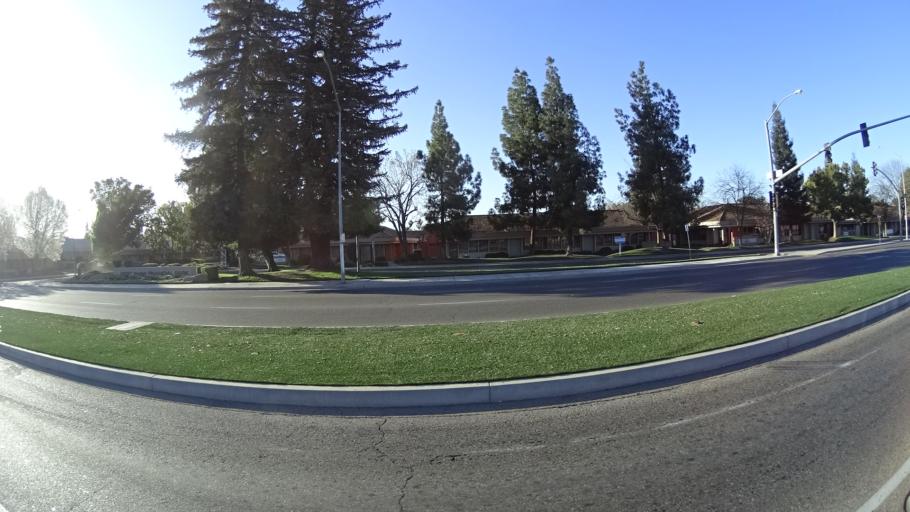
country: US
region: California
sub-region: Fresno County
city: Fresno
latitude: 36.8084
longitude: -119.8380
